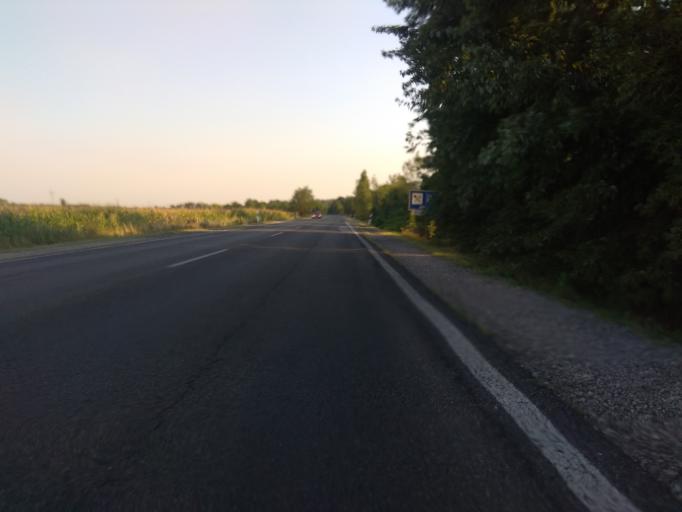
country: HU
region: Borsod-Abauj-Zemplen
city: Nyekladhaza
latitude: 47.9800
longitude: 20.8306
